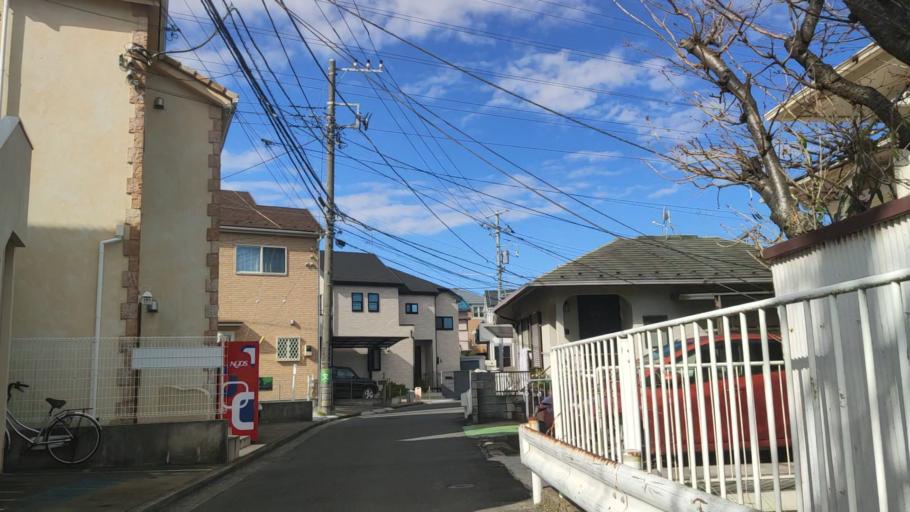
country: JP
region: Kanagawa
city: Yokohama
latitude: 35.4699
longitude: 139.5836
